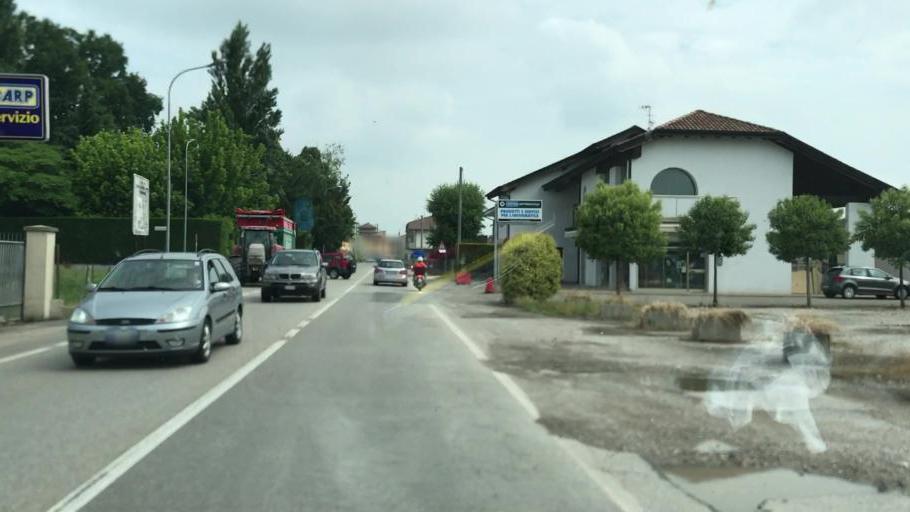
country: IT
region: Lombardy
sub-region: Provincia di Mantova
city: Poggio Rusco
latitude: 44.9754
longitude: 11.1143
